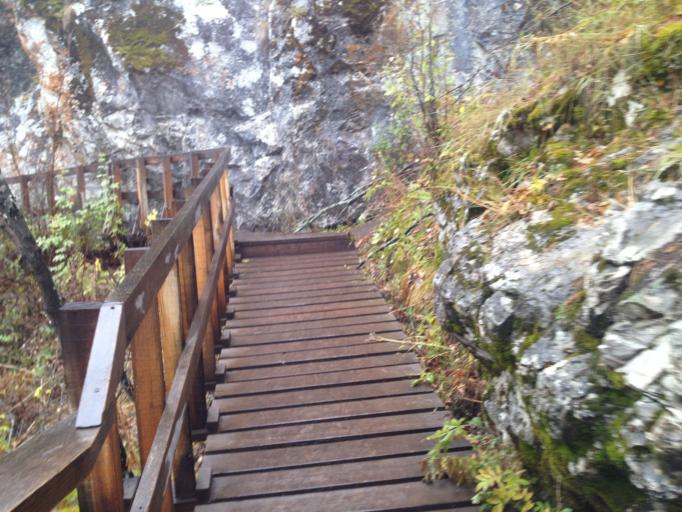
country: RU
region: Sverdlovsk
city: Nizhniye Sergi
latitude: 56.5178
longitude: 59.2555
